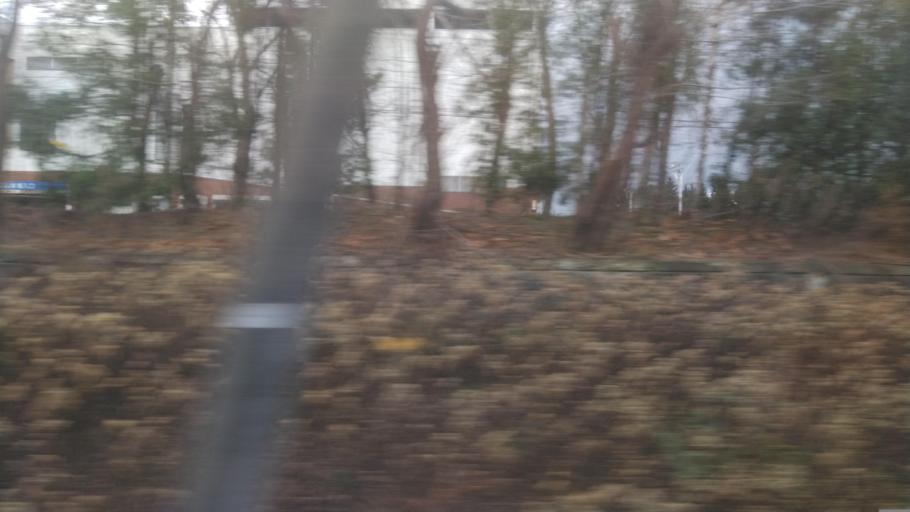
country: JP
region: Hokkaido
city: Kitahiroshima
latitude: 42.9750
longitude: 141.5637
